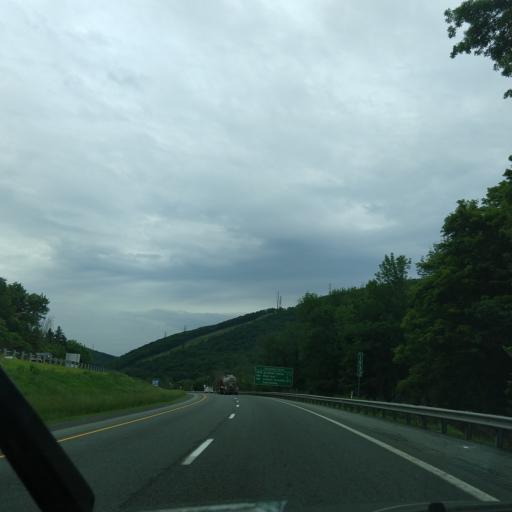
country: US
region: Pennsylvania
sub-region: Lackawanna County
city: Chinchilla
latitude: 41.4755
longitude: -75.6816
